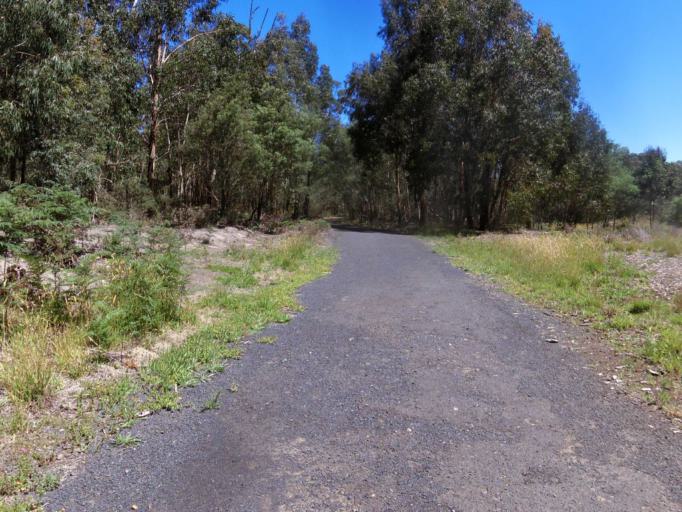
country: AU
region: Victoria
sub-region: Whittlesea
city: Whittlesea
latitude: -37.3591
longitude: 145.0341
